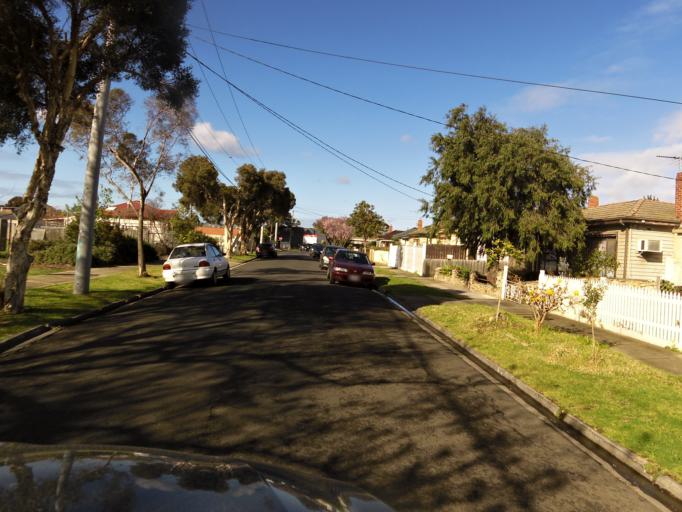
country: AU
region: Victoria
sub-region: Maribyrnong
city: Kingsville
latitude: -37.8097
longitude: 144.8666
